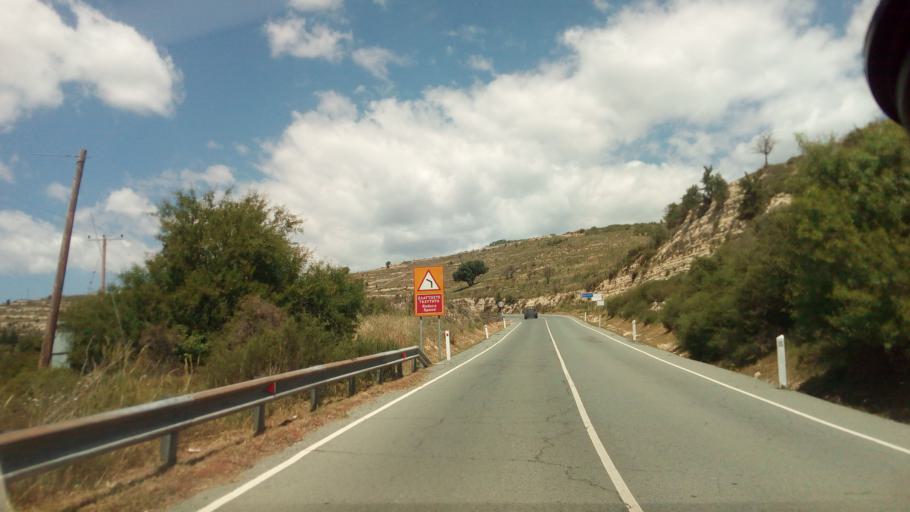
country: CY
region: Limassol
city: Pachna
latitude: 34.7878
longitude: 32.8243
